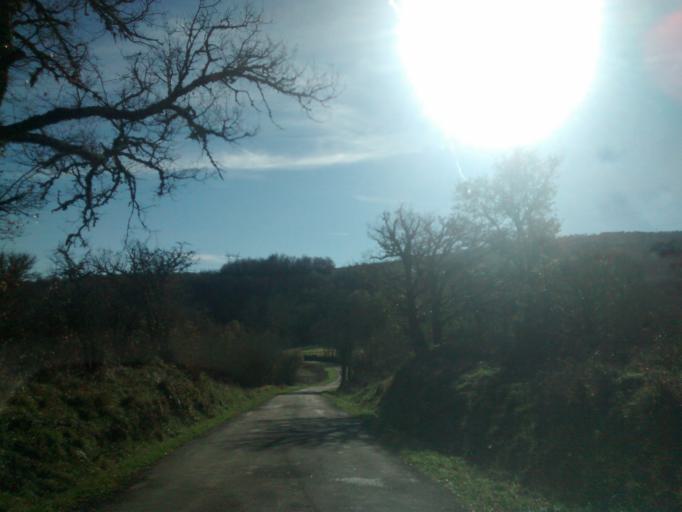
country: ES
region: Cantabria
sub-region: Provincia de Cantabria
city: San Pedro del Romeral
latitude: 42.9671
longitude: -3.7530
